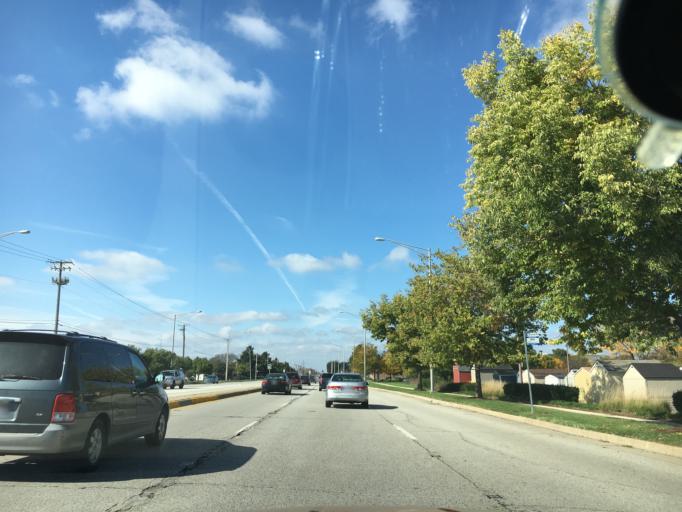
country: US
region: Illinois
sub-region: Cook County
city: Tinley Park
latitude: 41.6024
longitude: -87.7966
